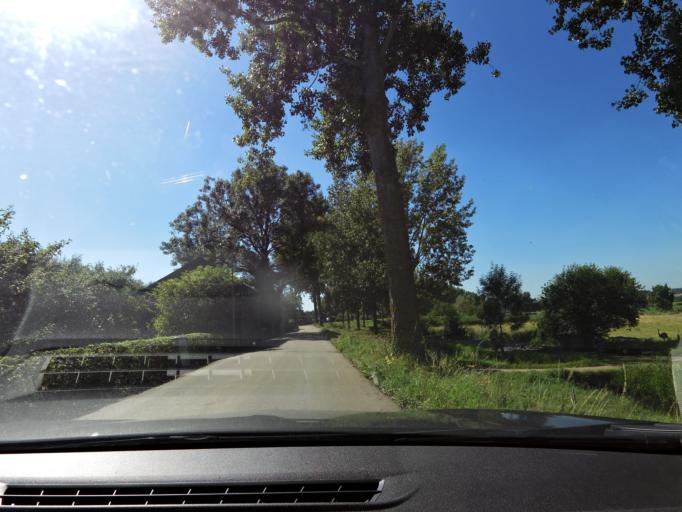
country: NL
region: South Holland
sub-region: Gemeente Dordrecht
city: Dordrecht
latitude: 51.7846
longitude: 4.6996
